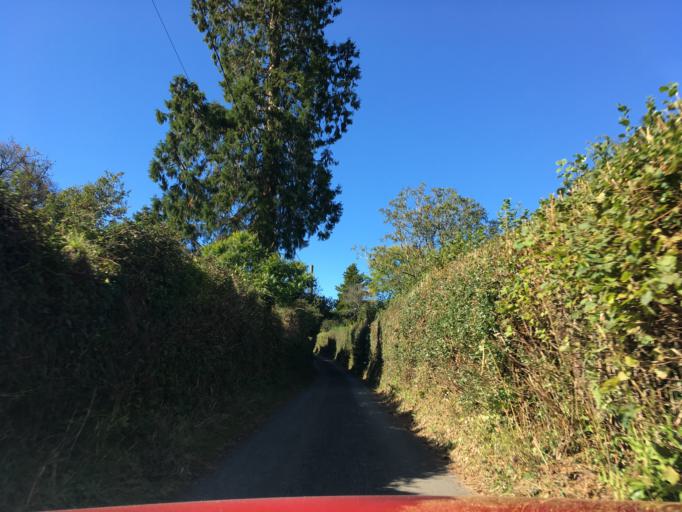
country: GB
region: Wales
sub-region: Torfaen County Borough
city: Cwmbran
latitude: 51.6251
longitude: -3.0452
